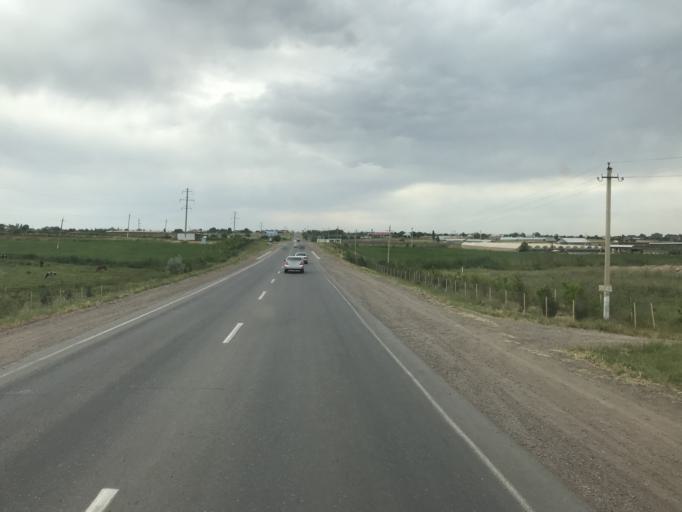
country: KZ
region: Ongtustik Qazaqstan
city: Saryaghash
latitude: 41.4537
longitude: 69.1356
